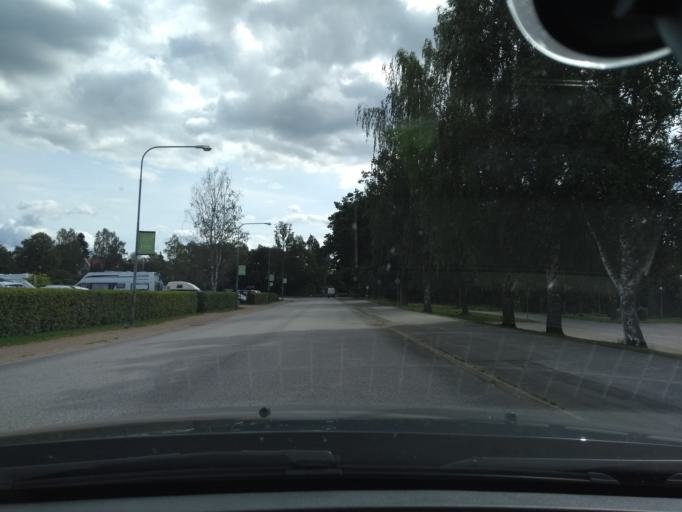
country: SE
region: Kalmar
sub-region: Vimmerby Kommun
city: Vimmerby
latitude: 57.6740
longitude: 15.8562
